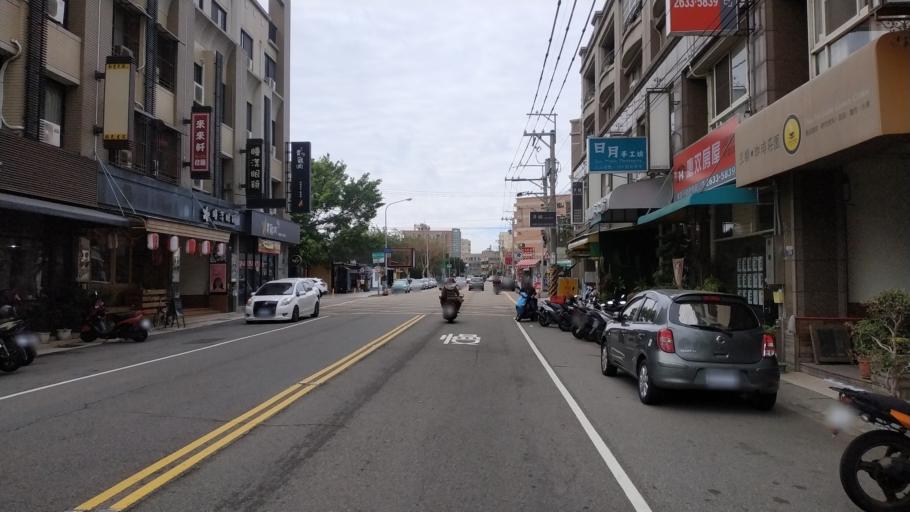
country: TW
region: Taiwan
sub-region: Taichung City
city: Taichung
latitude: 24.2297
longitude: 120.5714
